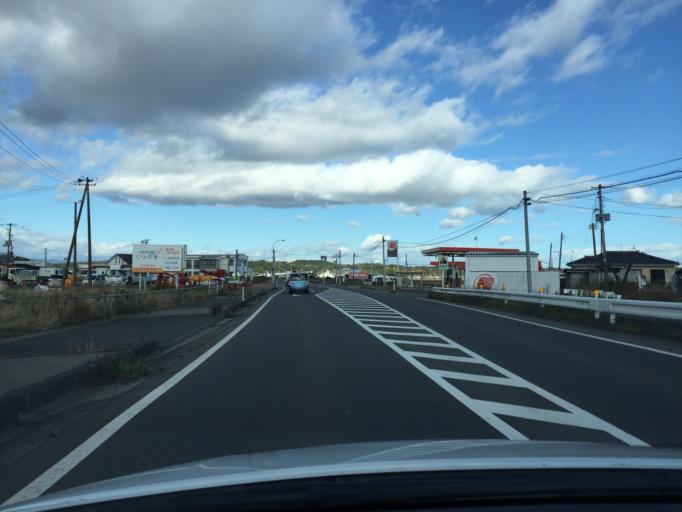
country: JP
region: Fukushima
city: Namie
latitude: 37.5538
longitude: 141.0056
